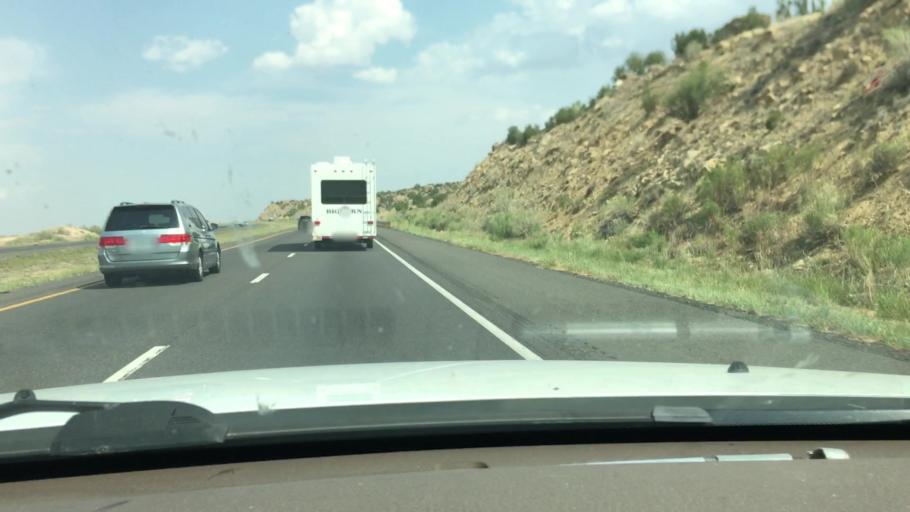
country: US
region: New Mexico
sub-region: Cibola County
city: Laguna
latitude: 35.0403
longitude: -107.4954
